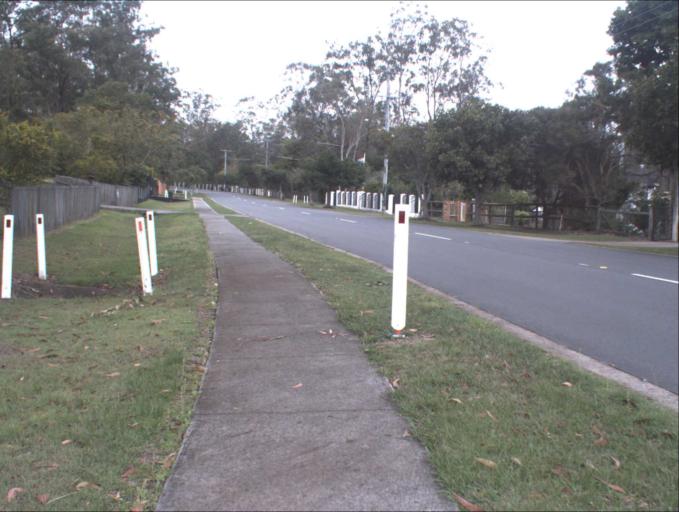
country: AU
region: Queensland
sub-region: Brisbane
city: Forest Lake
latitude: -27.6677
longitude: 152.9984
